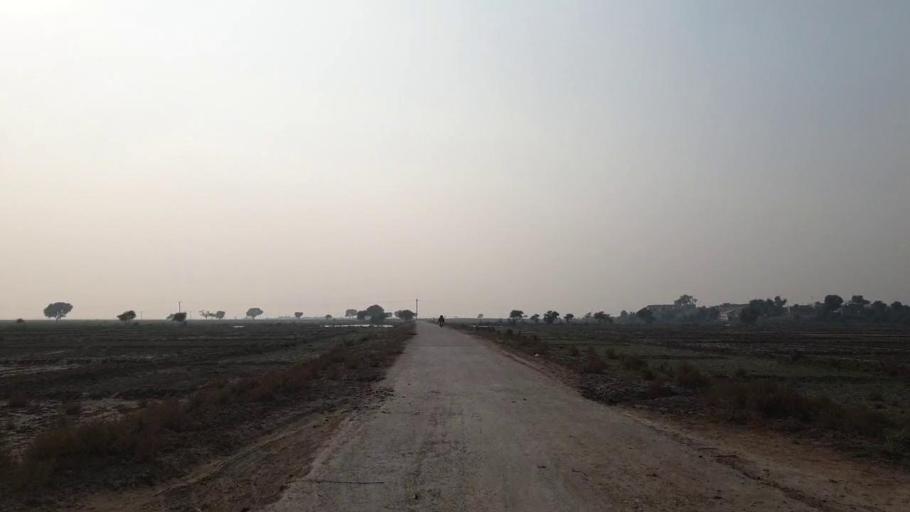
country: PK
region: Sindh
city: Bhan
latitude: 26.4879
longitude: 67.7082
